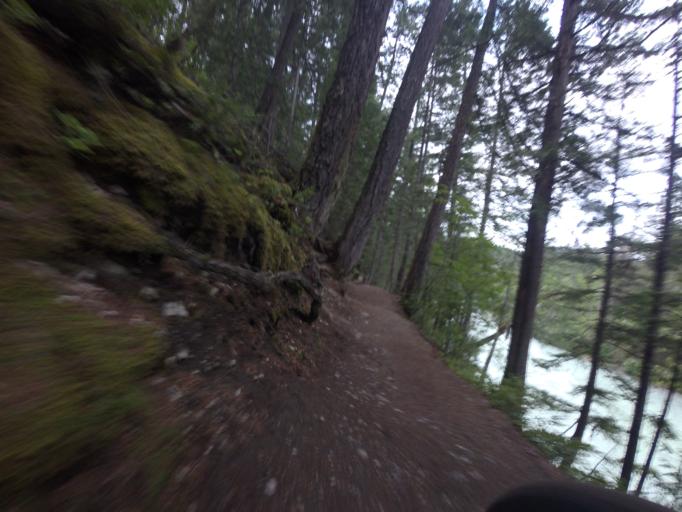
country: CA
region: British Columbia
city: Pemberton
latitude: 50.2951
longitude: -122.8246
